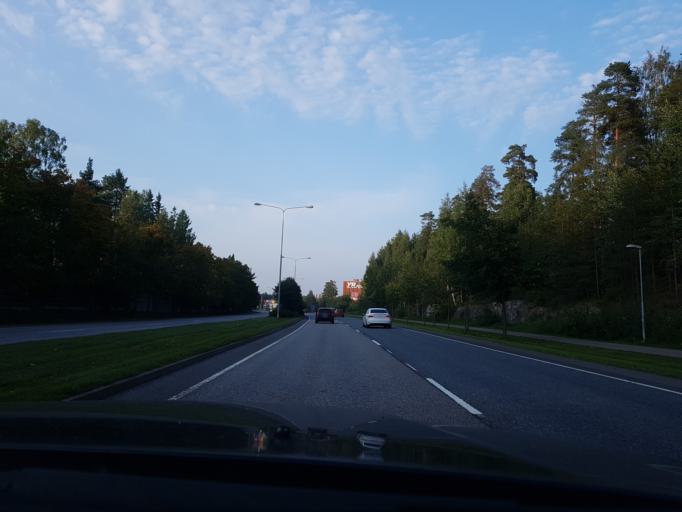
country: FI
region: Uusimaa
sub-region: Helsinki
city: Tuusula
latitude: 60.3802
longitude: 25.0243
